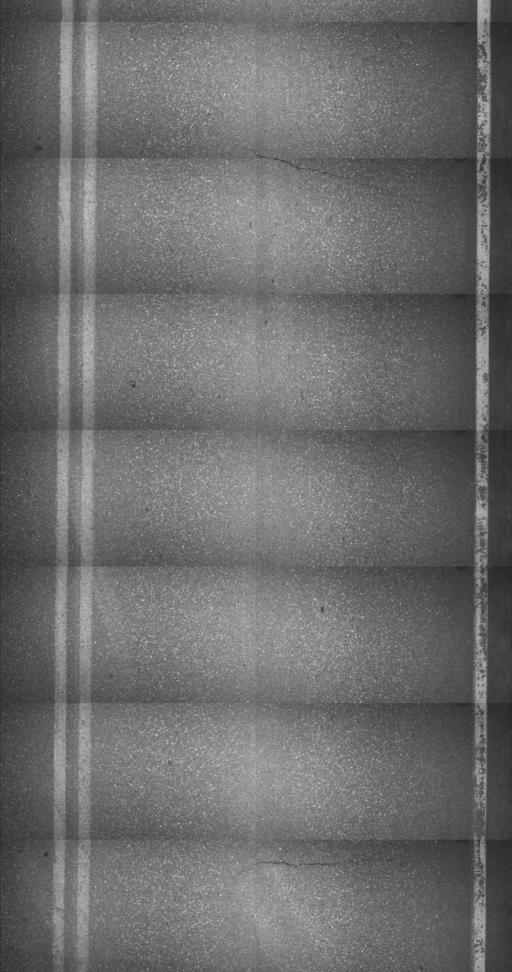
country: US
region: Vermont
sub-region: Orleans County
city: Newport
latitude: 44.9420
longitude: -72.0961
